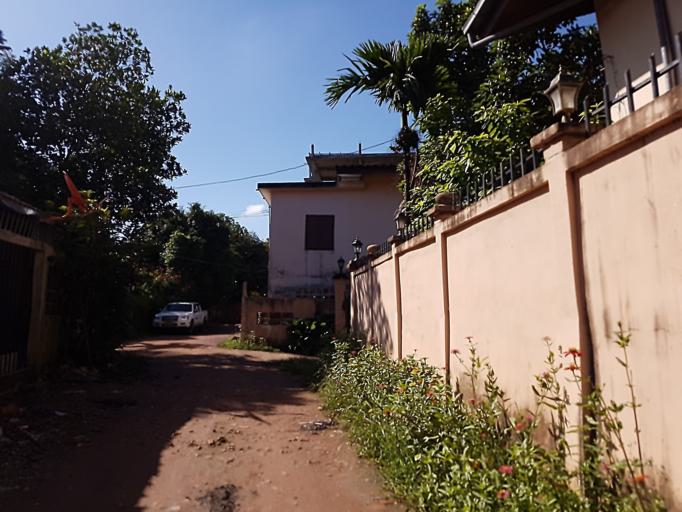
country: TH
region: Nong Khai
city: Si Chiang Mai
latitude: 17.9248
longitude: 102.6158
